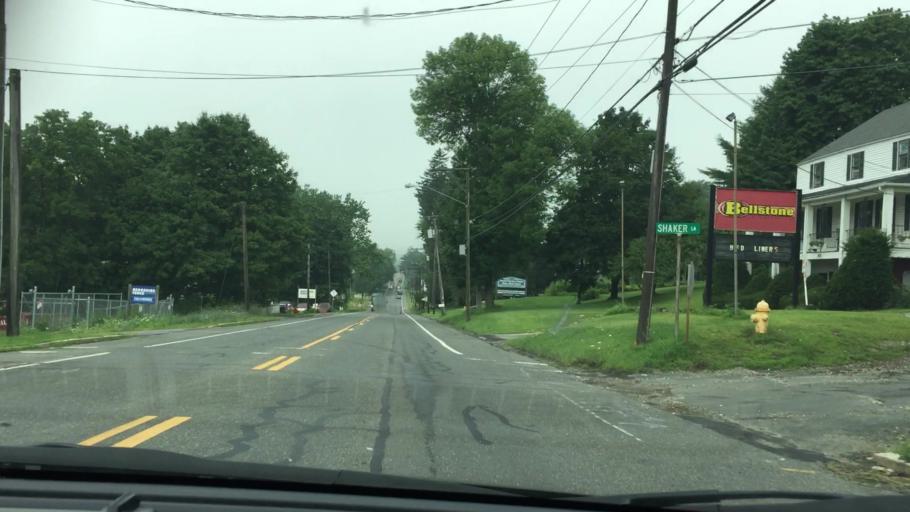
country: US
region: Massachusetts
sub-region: Berkshire County
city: Richmond
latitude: 42.4314
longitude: -73.3233
